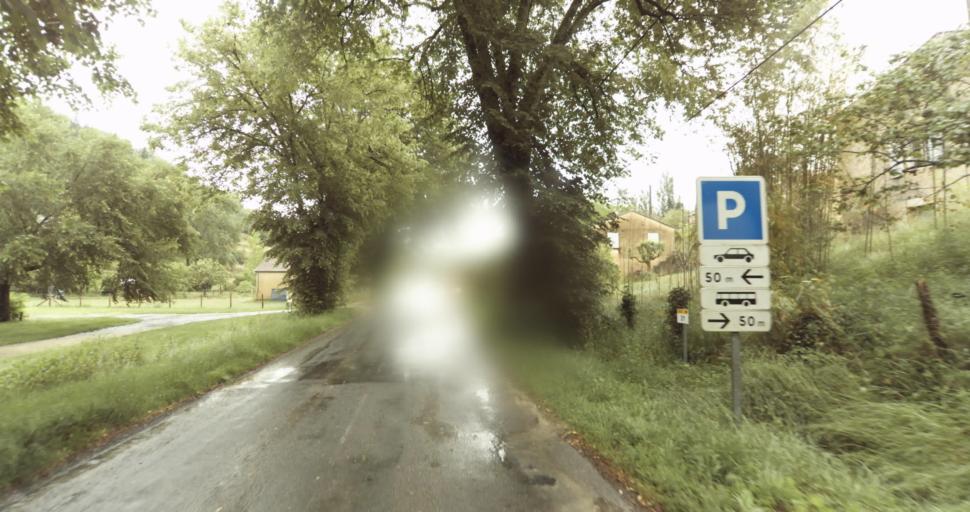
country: FR
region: Aquitaine
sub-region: Departement de la Dordogne
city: Beaumont-du-Perigord
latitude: 44.8118
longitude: 0.8691
